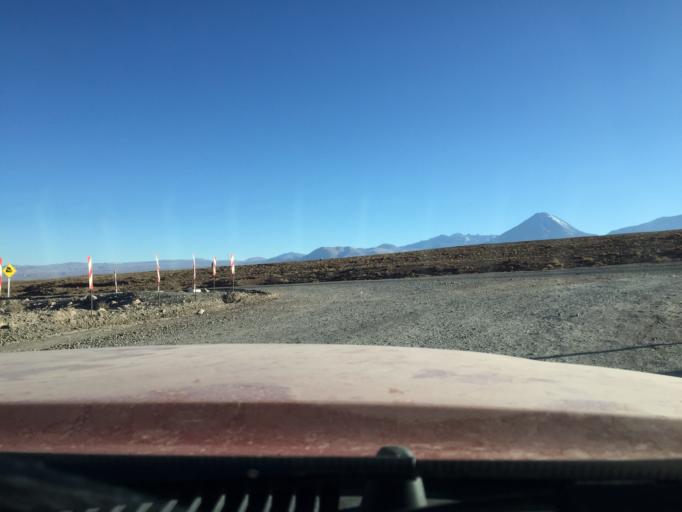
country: CL
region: Antofagasta
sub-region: Provincia de El Loa
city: San Pedro de Atacama
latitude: -23.0697
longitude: -67.9829
